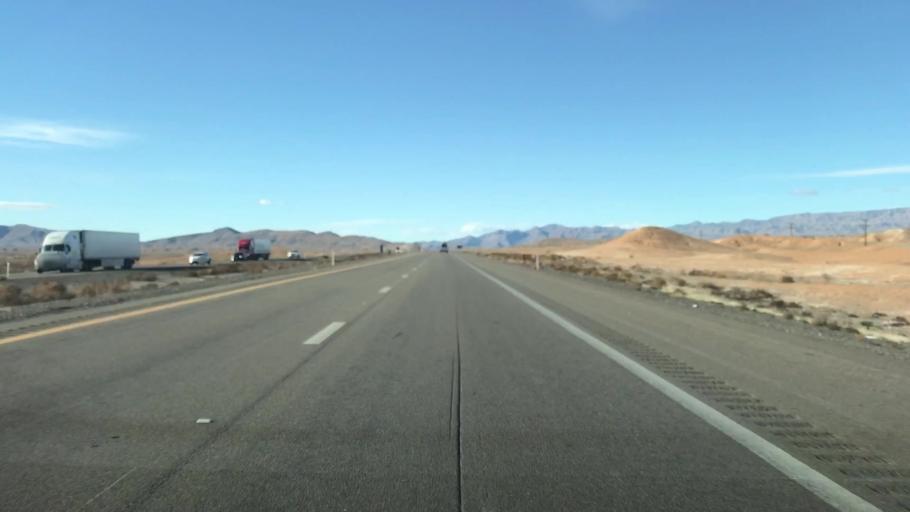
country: US
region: Nevada
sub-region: Clark County
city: Moapa Town
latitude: 36.4952
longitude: -114.7761
